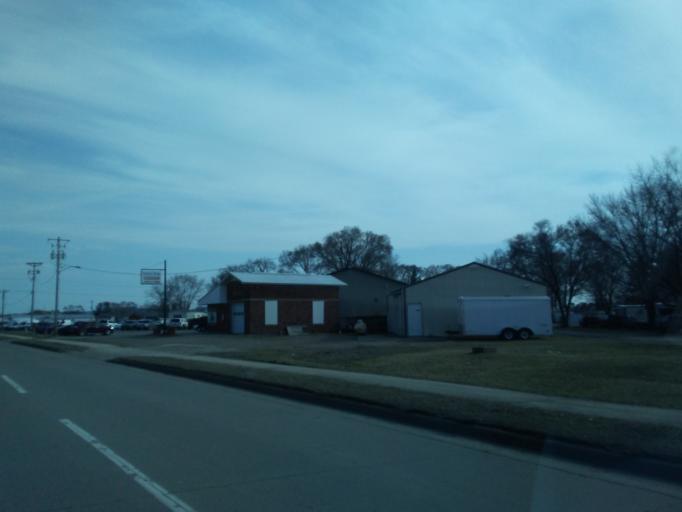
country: US
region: Wisconsin
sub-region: Crawford County
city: Prairie du Chien
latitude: 43.0336
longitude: -91.1359
